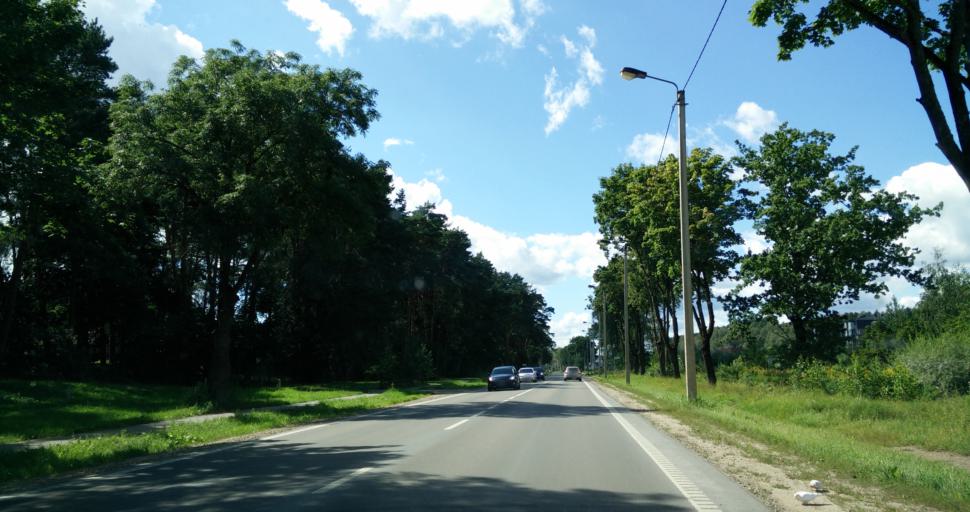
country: LT
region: Kauno apskritis
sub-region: Kauno rajonas
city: Akademija (Kaunas)
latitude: 54.9207
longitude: 23.8155
